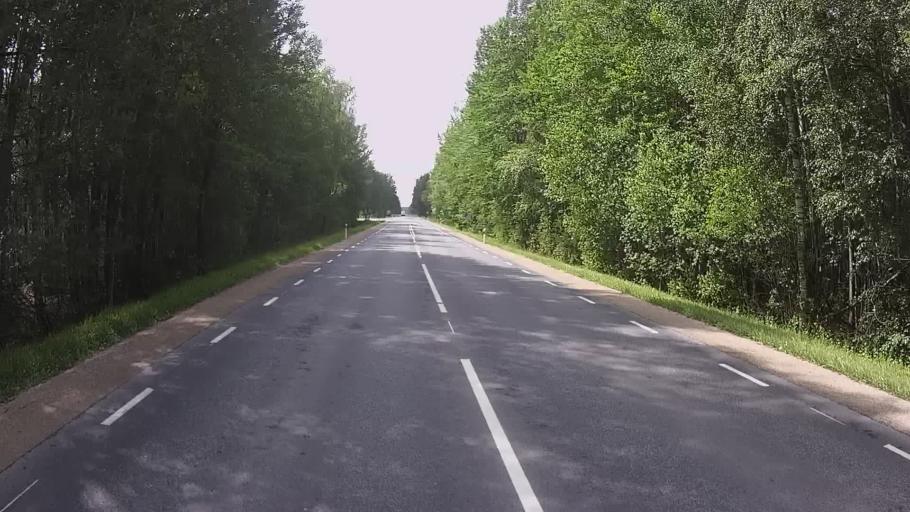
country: EE
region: Polvamaa
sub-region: Polva linn
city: Polva
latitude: 58.0625
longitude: 27.0815
